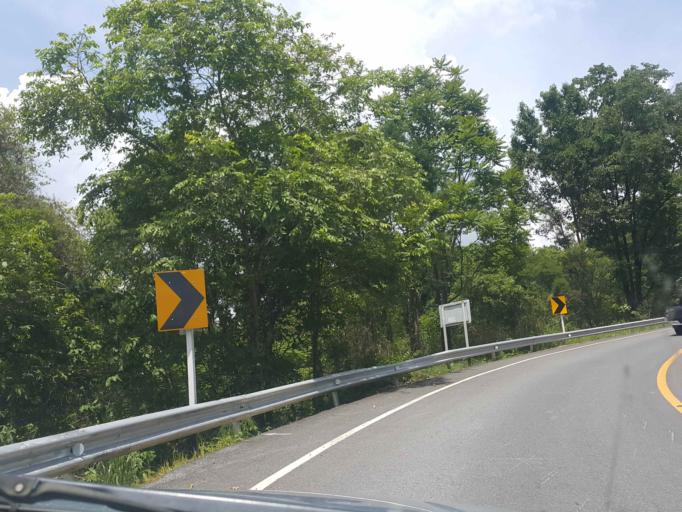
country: TH
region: Phayao
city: Chiang Muan
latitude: 18.8493
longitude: 100.3327
